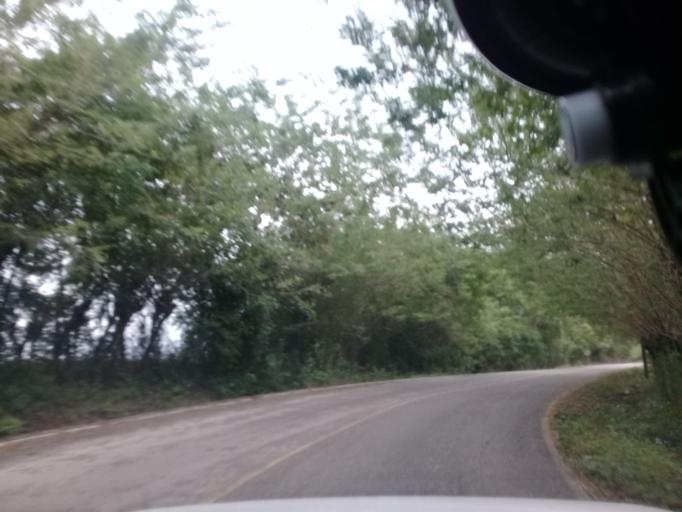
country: MX
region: Veracruz
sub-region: Chalma
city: San Pedro Coyutla
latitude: 21.2127
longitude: -98.4244
